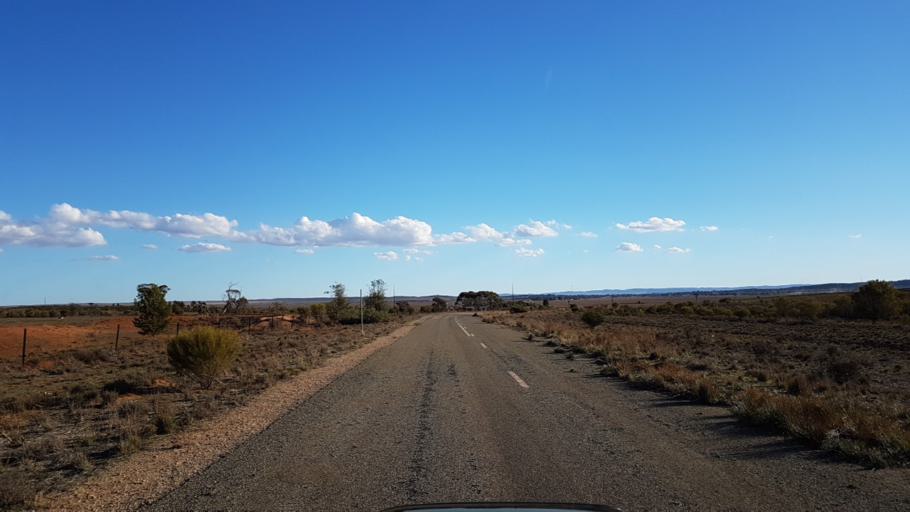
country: AU
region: South Australia
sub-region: Peterborough
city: Peterborough
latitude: -32.9591
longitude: 138.8945
